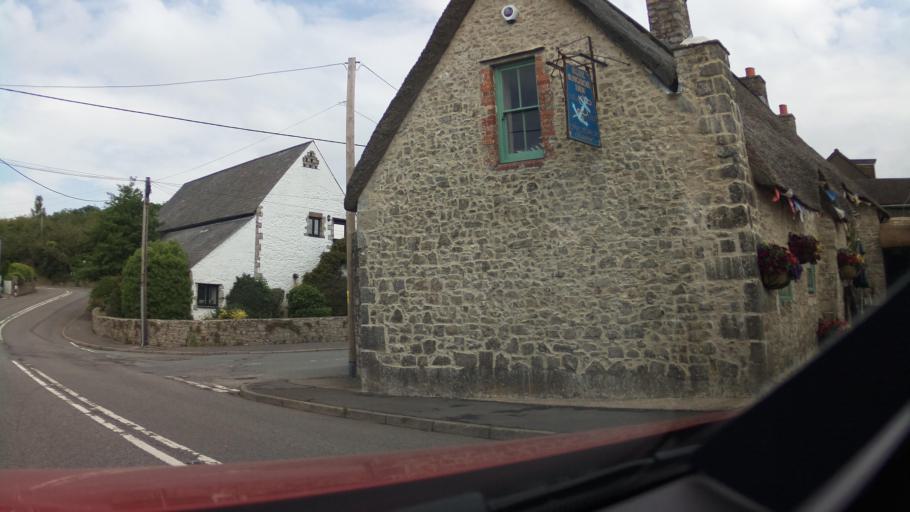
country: GB
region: Wales
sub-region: Vale of Glamorgan
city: Rhoose
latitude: 51.3907
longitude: -3.3886
